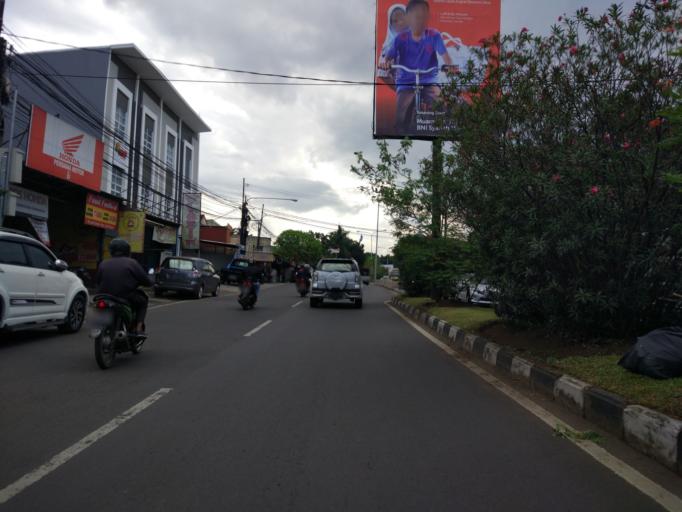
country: ID
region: West Java
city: Bandung
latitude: -6.9137
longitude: 107.6600
